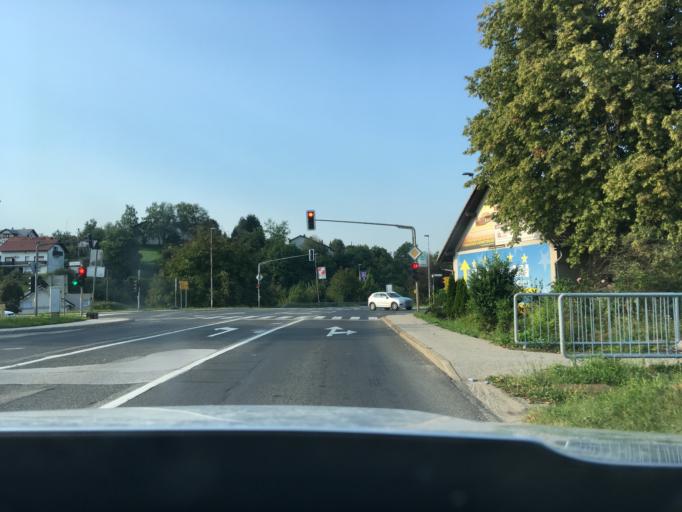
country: SI
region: Novo Mesto
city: Novo Mesto
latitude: 45.7991
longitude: 15.1801
